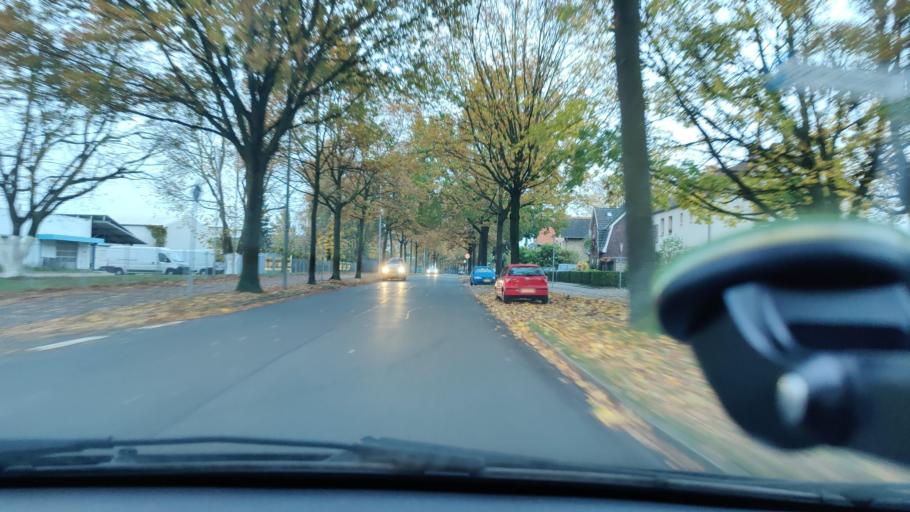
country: DE
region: North Rhine-Westphalia
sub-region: Regierungsbezirk Dusseldorf
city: Wesel
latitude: 51.6672
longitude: 6.6385
